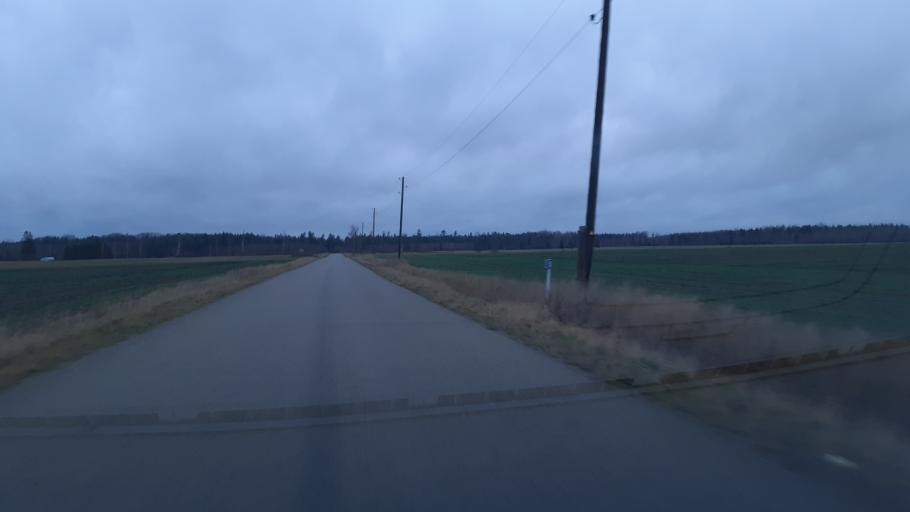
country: LV
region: Kuldigas Rajons
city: Kuldiga
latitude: 57.0261
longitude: 22.1678
